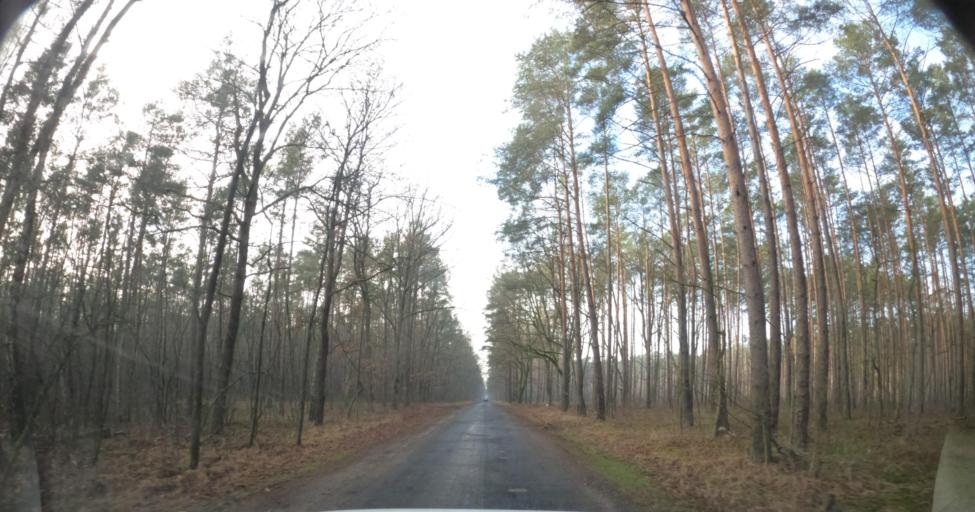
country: PL
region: West Pomeranian Voivodeship
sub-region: Powiat mysliborski
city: Boleszkowice
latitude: 52.7043
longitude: 14.5342
